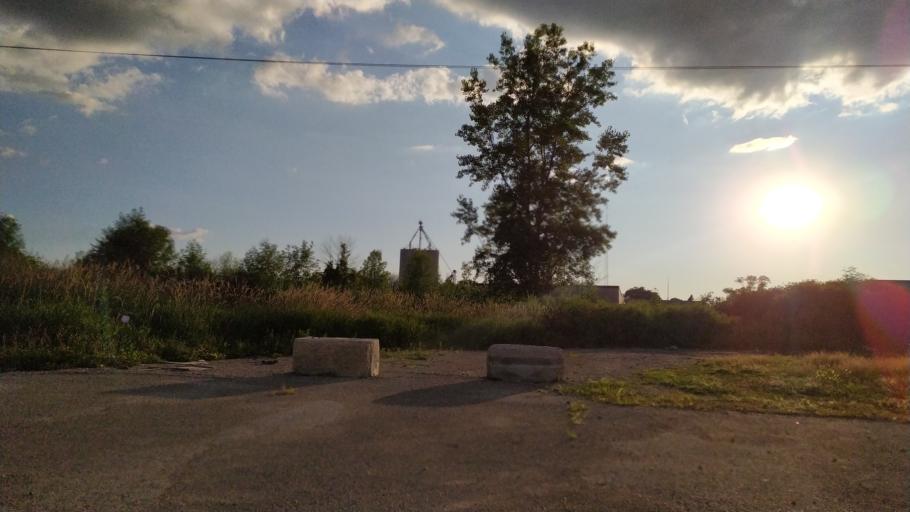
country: CA
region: Ontario
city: Stratford
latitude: 43.3647
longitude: -80.9549
